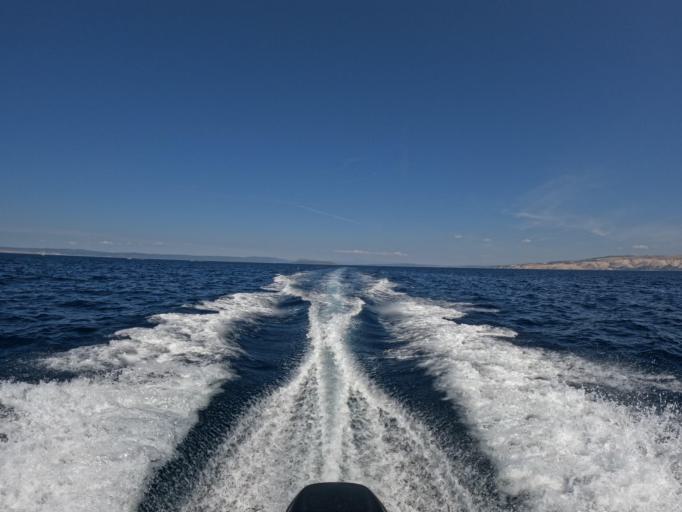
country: HR
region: Primorsko-Goranska
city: Lopar
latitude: 44.8831
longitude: 14.6544
